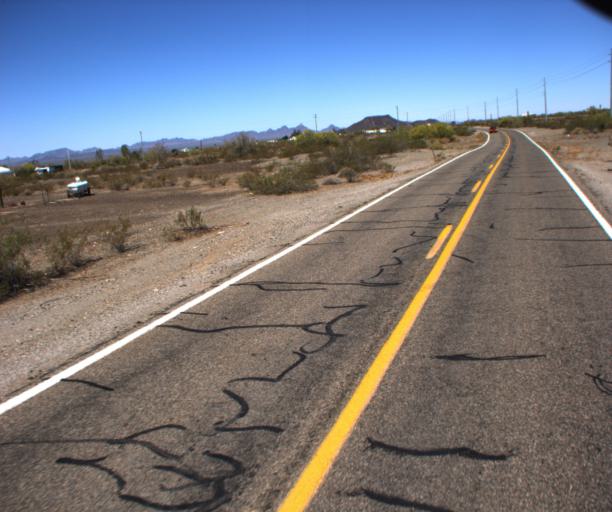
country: US
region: Arizona
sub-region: La Paz County
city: Salome
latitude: 33.7414
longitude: -113.7434
